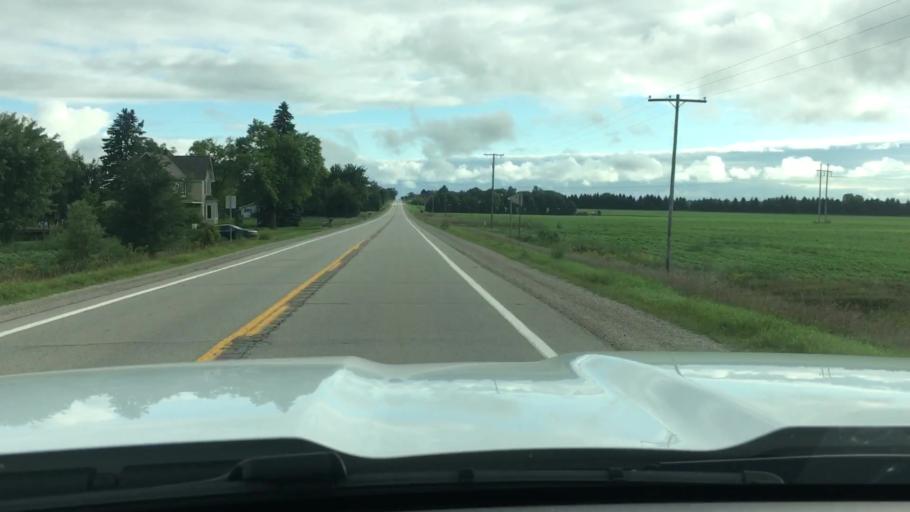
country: US
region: Michigan
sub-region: Tuscola County
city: Caro
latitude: 43.5407
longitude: -83.3382
